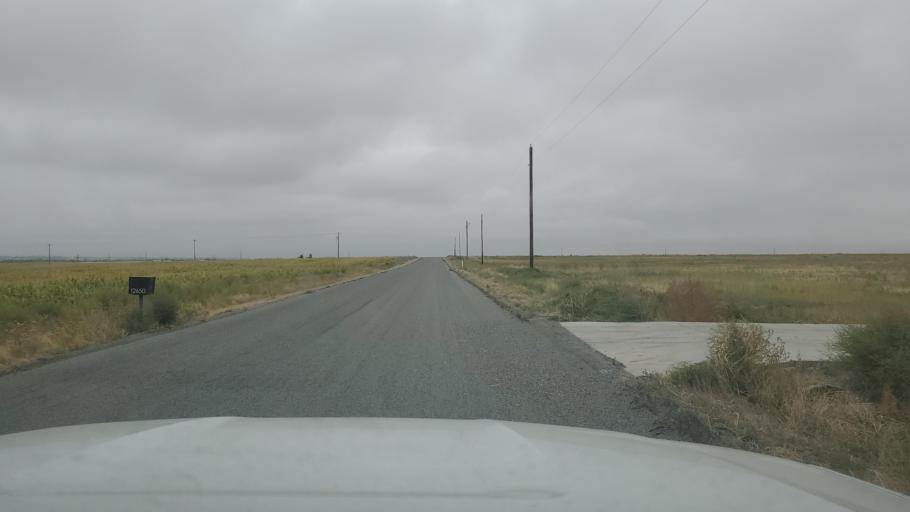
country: US
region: Colorado
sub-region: Weld County
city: Lochbuie
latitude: 39.9251
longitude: -104.6026
